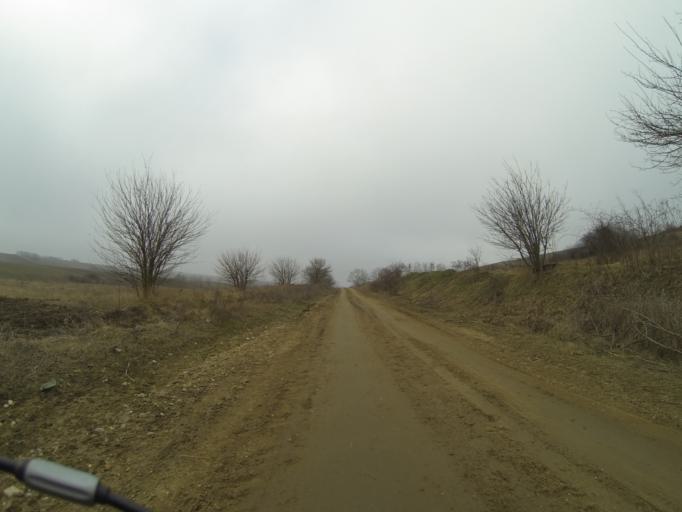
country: RO
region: Mehedinti
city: Padina Mica
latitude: 44.4877
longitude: 23.0187
